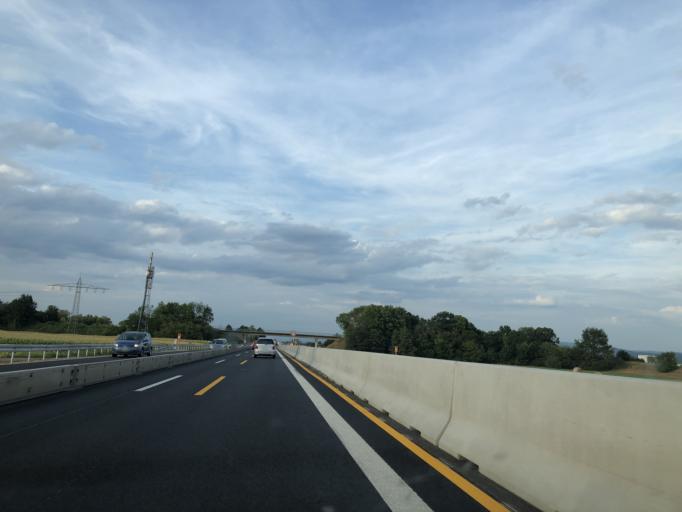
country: DE
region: Baden-Wuerttemberg
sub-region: Freiburg Region
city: Schwanau
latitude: 48.3759
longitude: 7.8136
